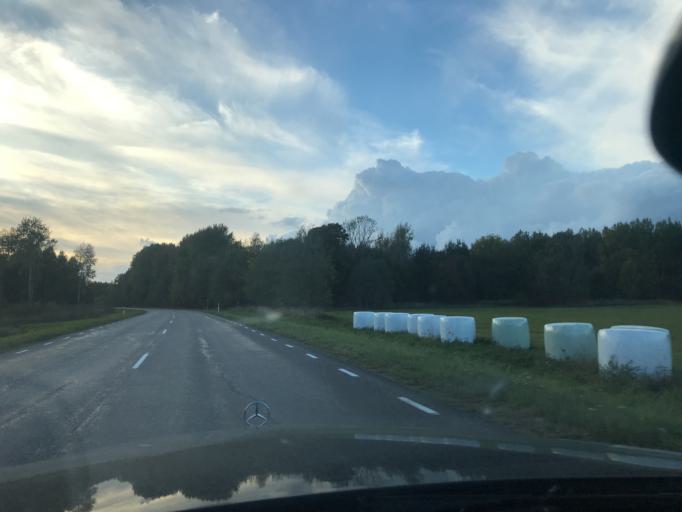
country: EE
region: Vorumaa
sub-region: Antsla vald
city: Vana-Antsla
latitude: 57.9042
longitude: 26.4599
